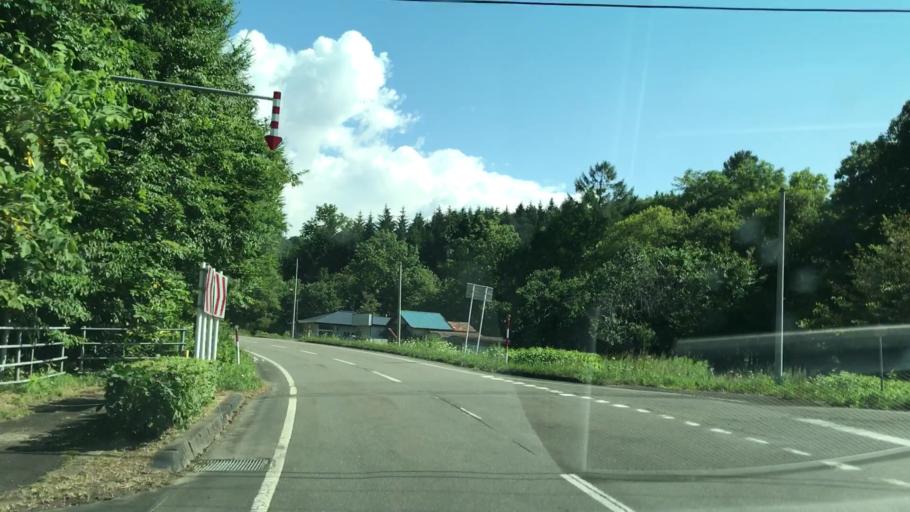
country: JP
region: Hokkaido
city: Shimo-furano
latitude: 42.8648
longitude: 142.4398
